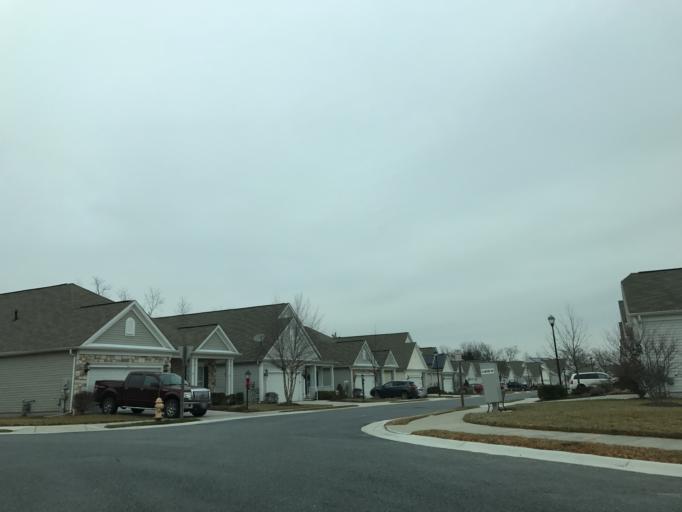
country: US
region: Maryland
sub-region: Carroll County
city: Taneytown
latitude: 39.6448
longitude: -77.1580
